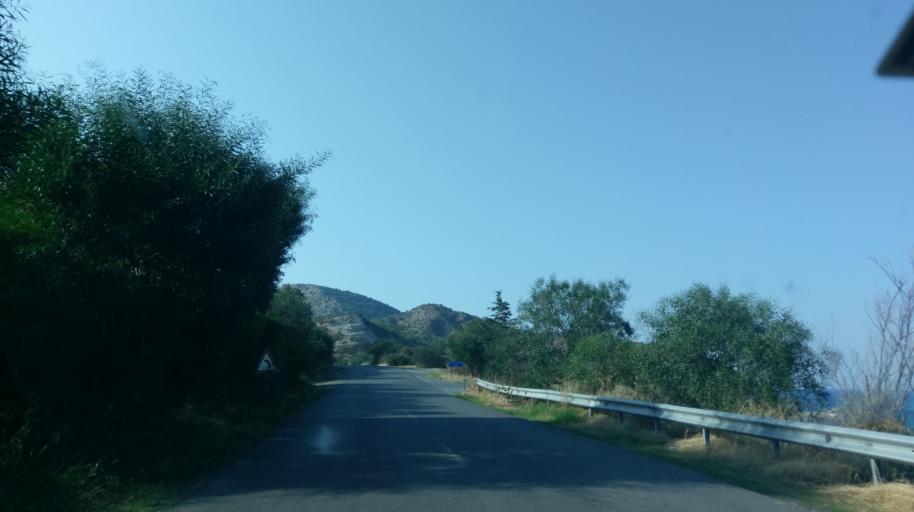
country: CY
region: Lefkosia
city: Lefka
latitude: 35.1540
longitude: 32.7912
